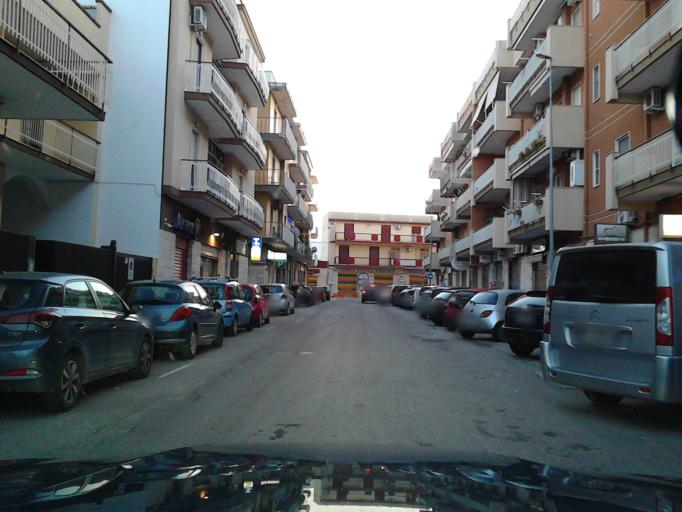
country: IT
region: Apulia
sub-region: Provincia di Bari
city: Valenzano
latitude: 41.0411
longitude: 16.8825
